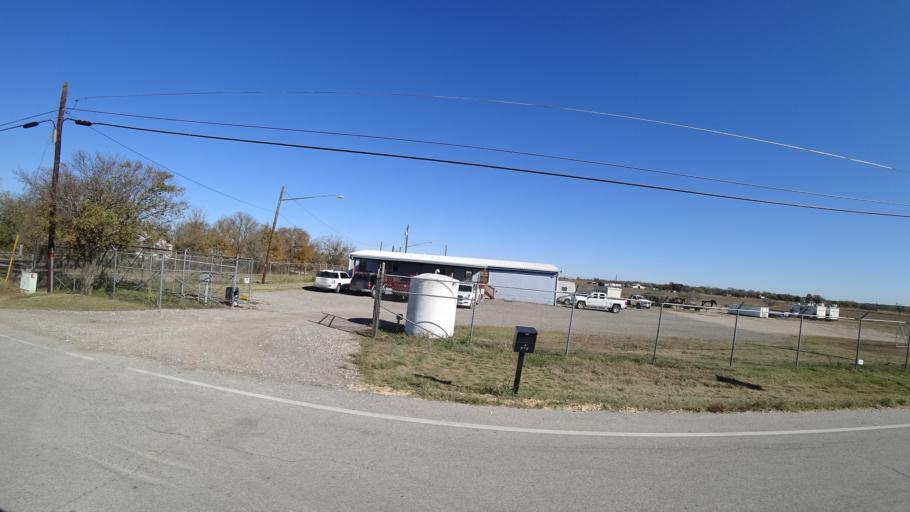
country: US
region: Texas
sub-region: Travis County
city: Garfield
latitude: 30.1147
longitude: -97.6528
